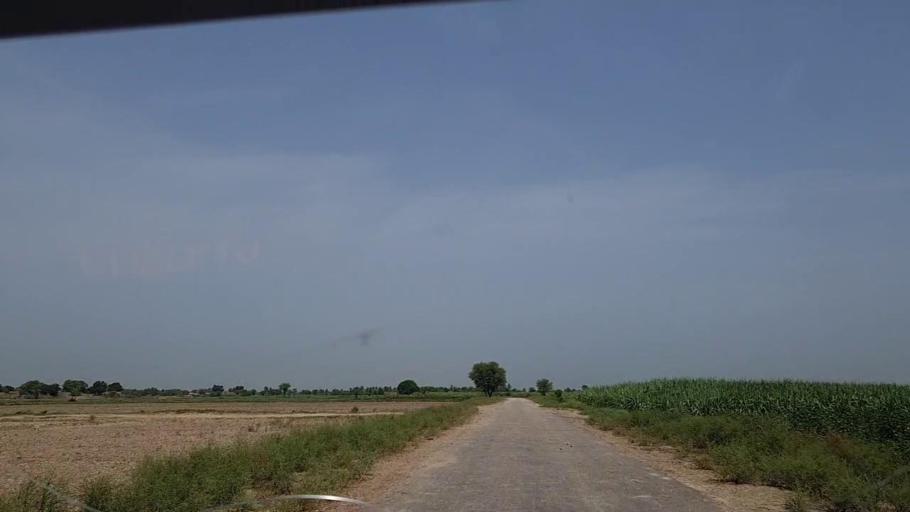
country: PK
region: Sindh
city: Tharu Shah
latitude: 26.9059
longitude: 68.0540
